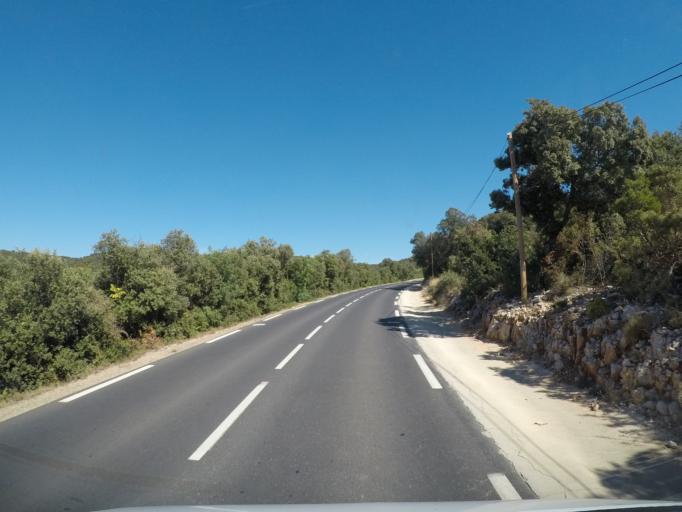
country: FR
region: Languedoc-Roussillon
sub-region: Departement de l'Herault
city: Aniane
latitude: 43.7206
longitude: 3.6245
